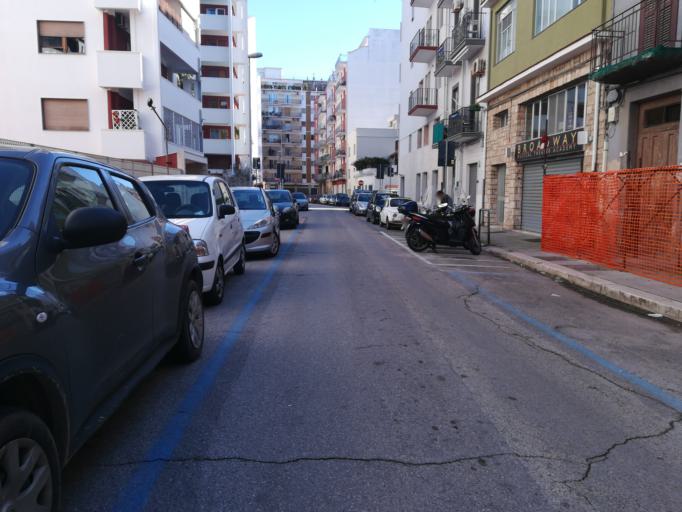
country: IT
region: Apulia
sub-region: Provincia di Bari
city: Bari
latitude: 41.1172
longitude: 16.8907
